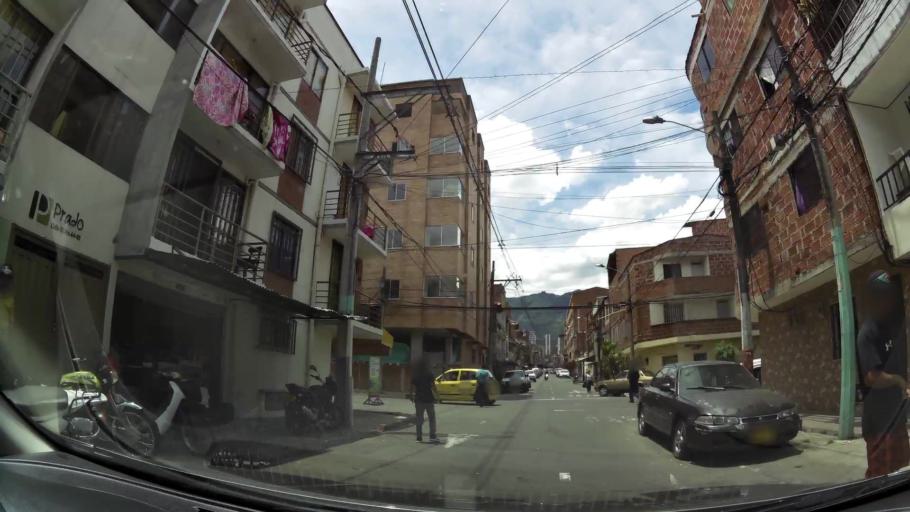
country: CO
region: Antioquia
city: Bello
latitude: 6.3366
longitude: -75.5541
